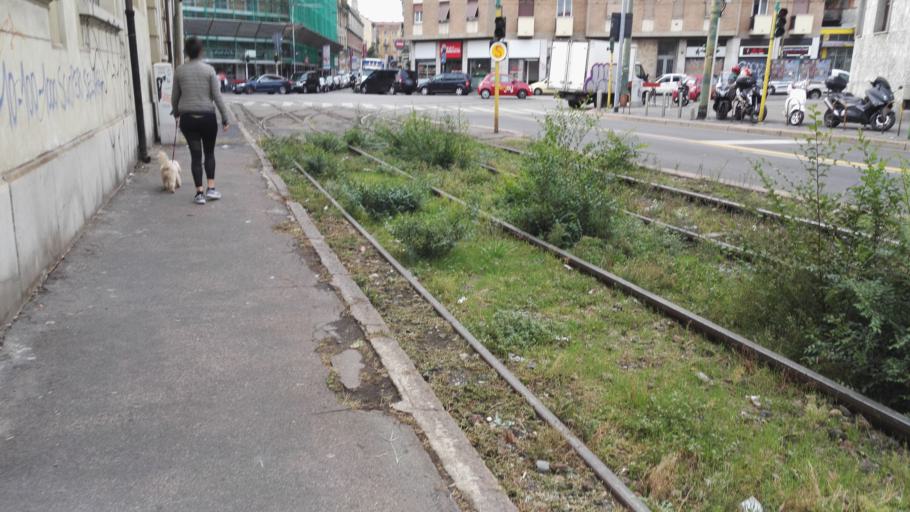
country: IT
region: Lombardy
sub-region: Citta metropolitana di Milano
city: Milano
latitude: 45.4843
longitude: 9.1746
